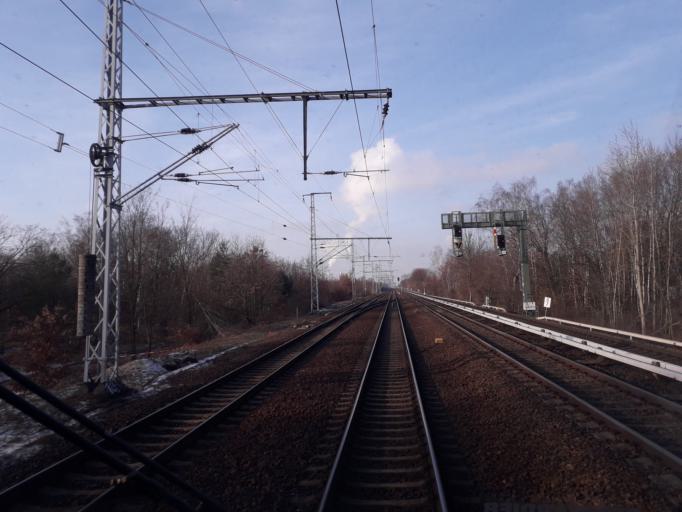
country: DE
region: Berlin
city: Karlshorst
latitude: 52.4727
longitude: 13.5447
